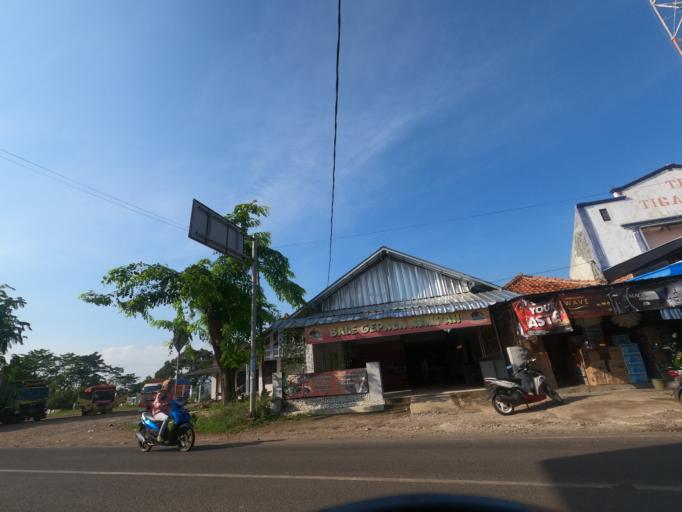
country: ID
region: West Java
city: Pamanukan
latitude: -6.5547
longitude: 107.8318
